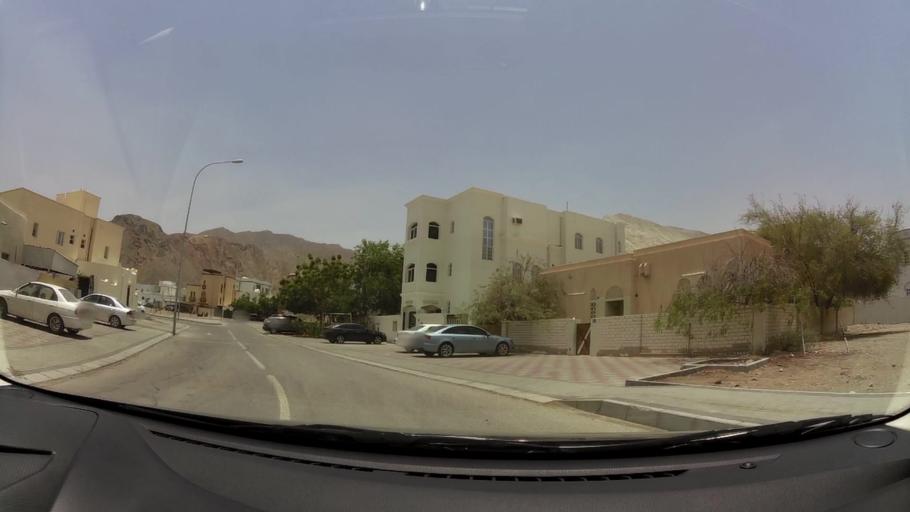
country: OM
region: Muhafazat Masqat
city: Bawshar
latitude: 23.5682
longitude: 58.4226
